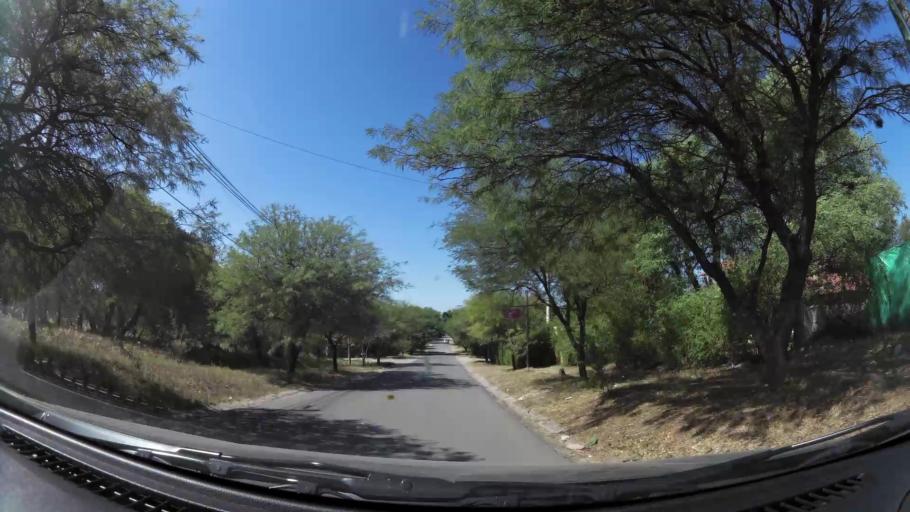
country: AR
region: Cordoba
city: Villa Allende
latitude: -31.2962
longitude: -64.2850
